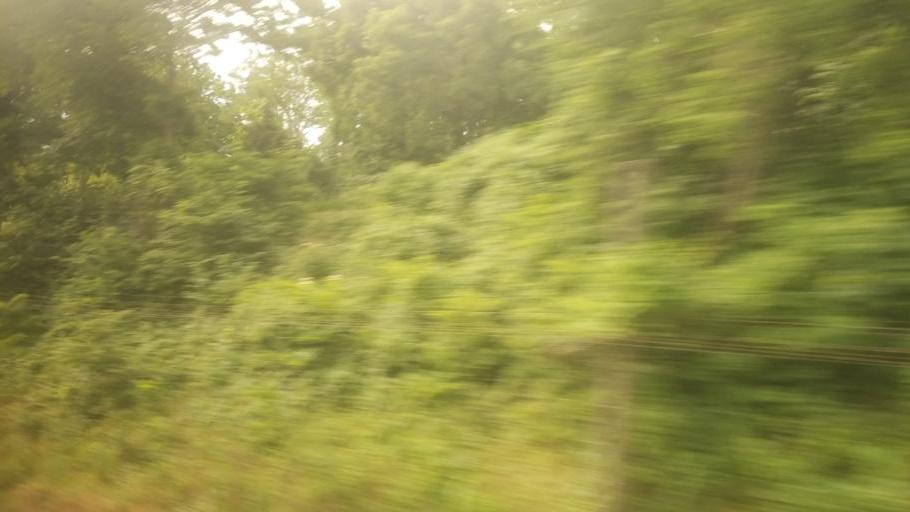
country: US
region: Kansas
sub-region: Jefferson County
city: Oskaloosa
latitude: 39.0585
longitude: -95.4142
